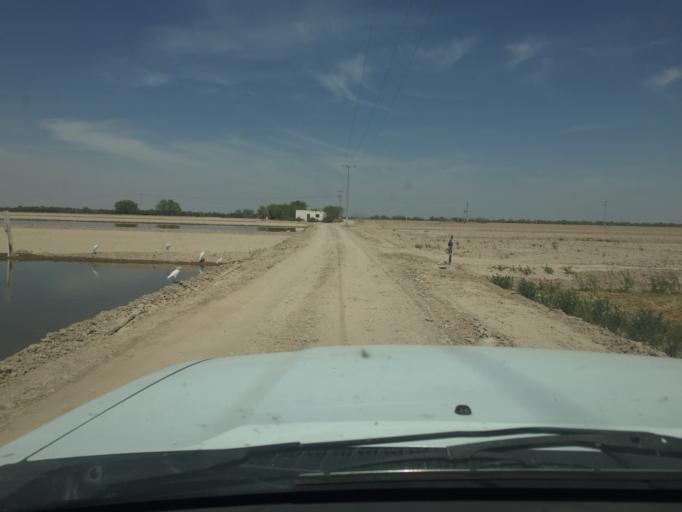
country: MX
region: Durango
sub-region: Gomez Palacio
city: El Vergel
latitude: 25.7379
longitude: -103.5058
